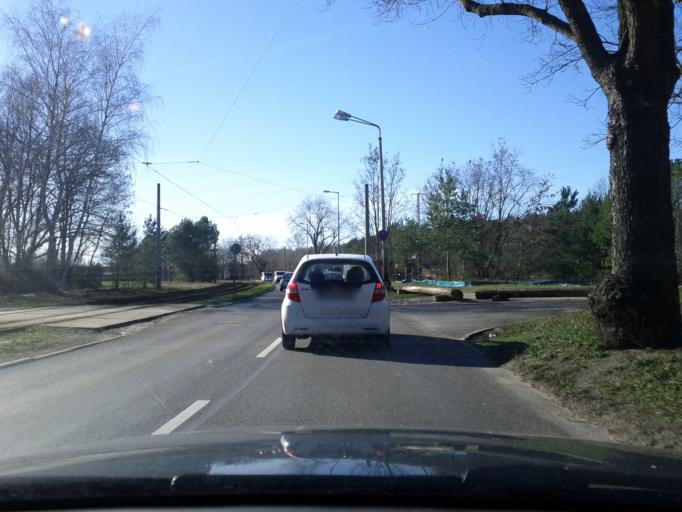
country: DE
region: Berlin
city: Friedrichshagen
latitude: 52.4557
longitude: 13.6447
